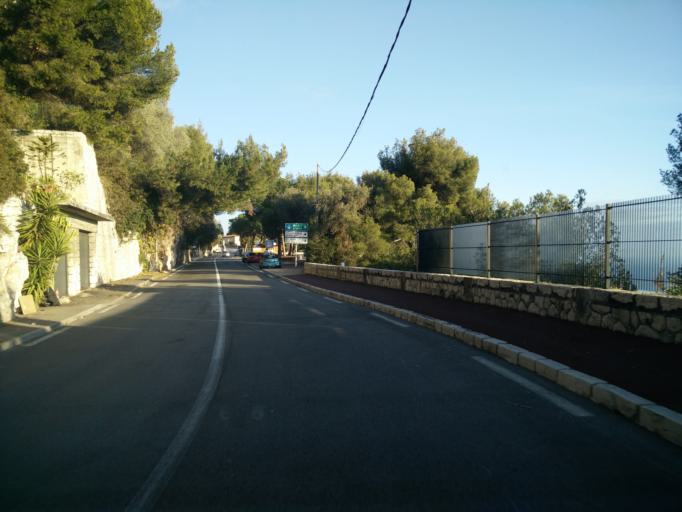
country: FR
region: Provence-Alpes-Cote d'Azur
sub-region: Departement des Alpes-Maritimes
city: Villefranche-sur-Mer
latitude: 43.7099
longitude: 7.3156
